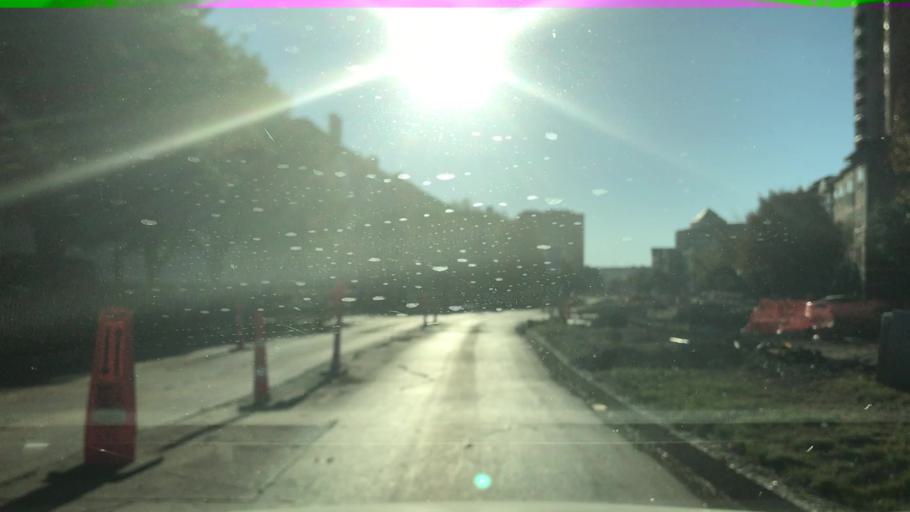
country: US
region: Texas
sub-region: Dallas County
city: Irving
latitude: 32.8669
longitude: -96.9388
